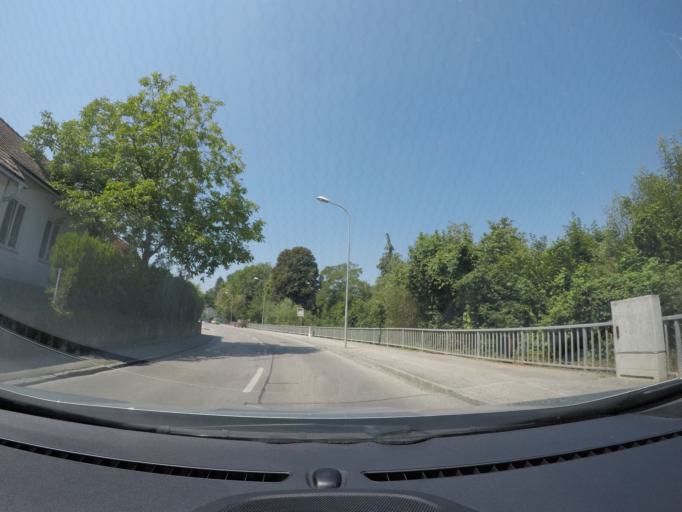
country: AT
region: Lower Austria
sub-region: Politischer Bezirk Sankt Polten
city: Eichgraben
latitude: 48.1845
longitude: 15.9616
